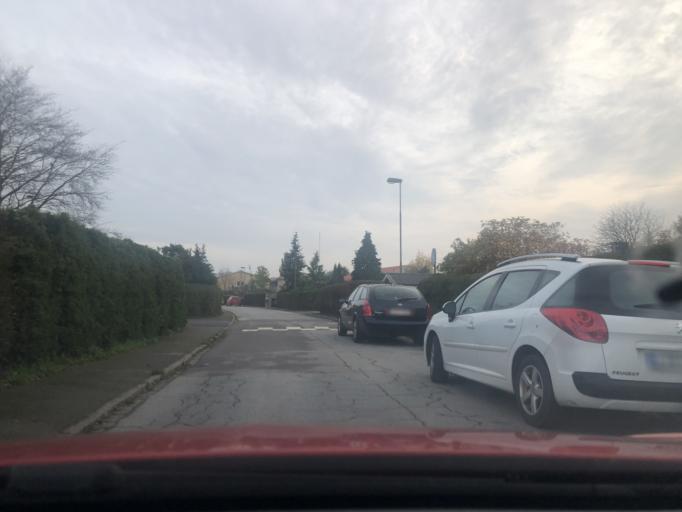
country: SE
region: Skane
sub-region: Burlovs Kommun
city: Arloev
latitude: 55.6017
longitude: 13.0790
